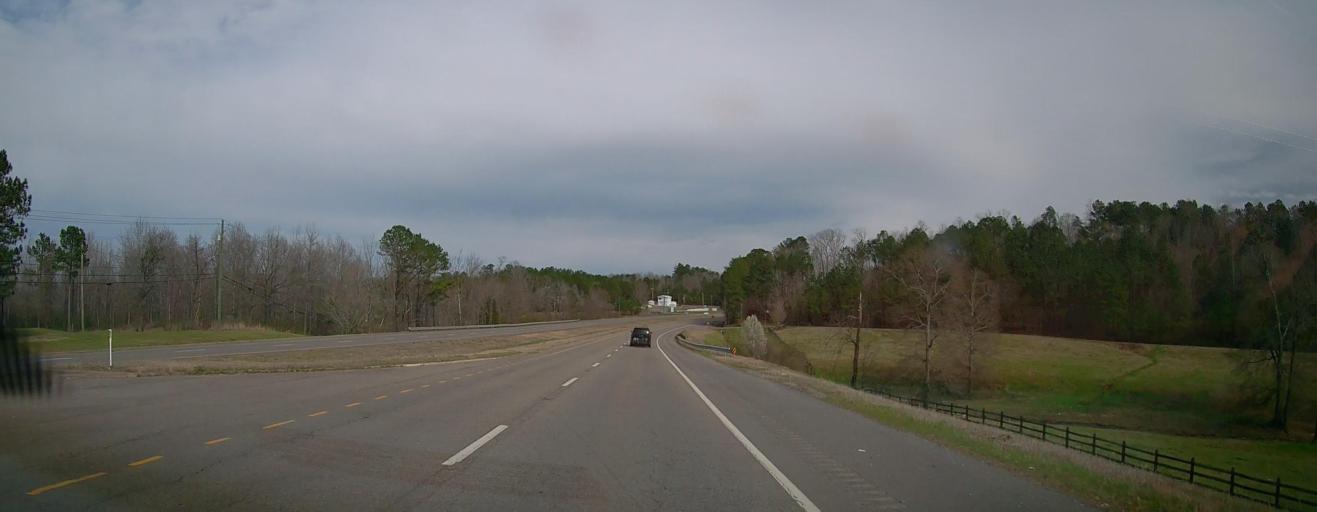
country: US
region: Alabama
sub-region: Walker County
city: Sumiton
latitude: 33.7943
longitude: -87.1010
